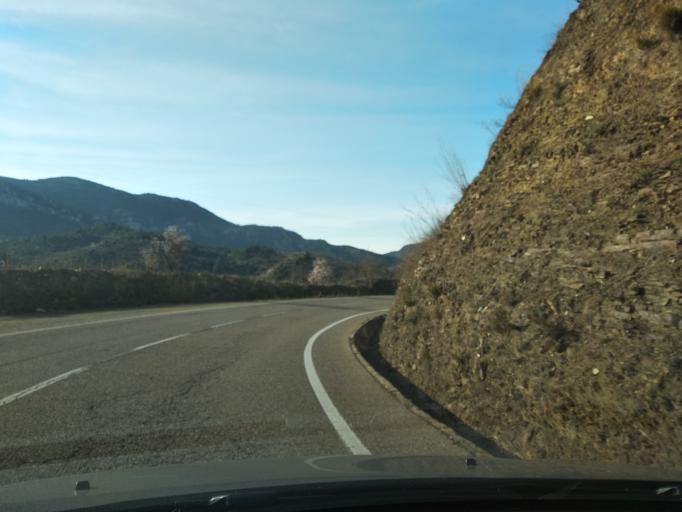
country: ES
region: Catalonia
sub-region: Provincia de Tarragona
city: Margalef
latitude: 41.2158
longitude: 0.7661
